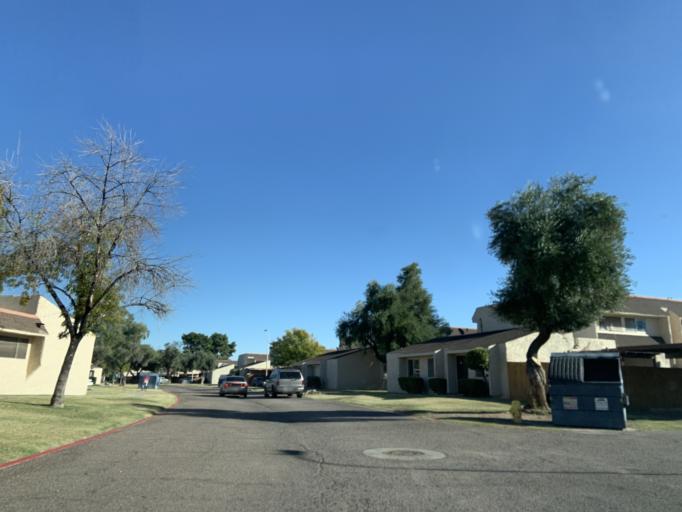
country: US
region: Arizona
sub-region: Maricopa County
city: Tempe
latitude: 33.3954
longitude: -111.8803
